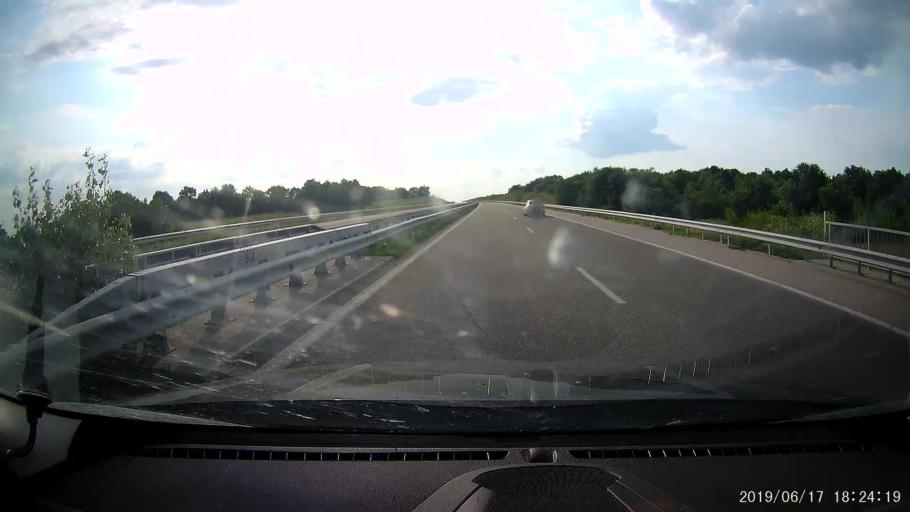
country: BG
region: Khaskovo
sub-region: Obshtina Dimitrovgrad
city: Dimitrovgrad
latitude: 41.9832
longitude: 25.6950
